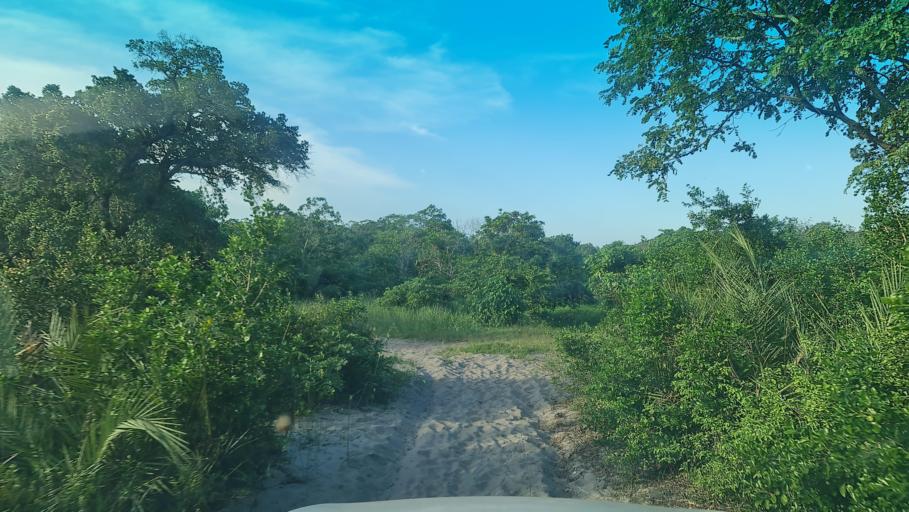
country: MZ
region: Gaza
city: Macia
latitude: -25.2302
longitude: 33.0144
